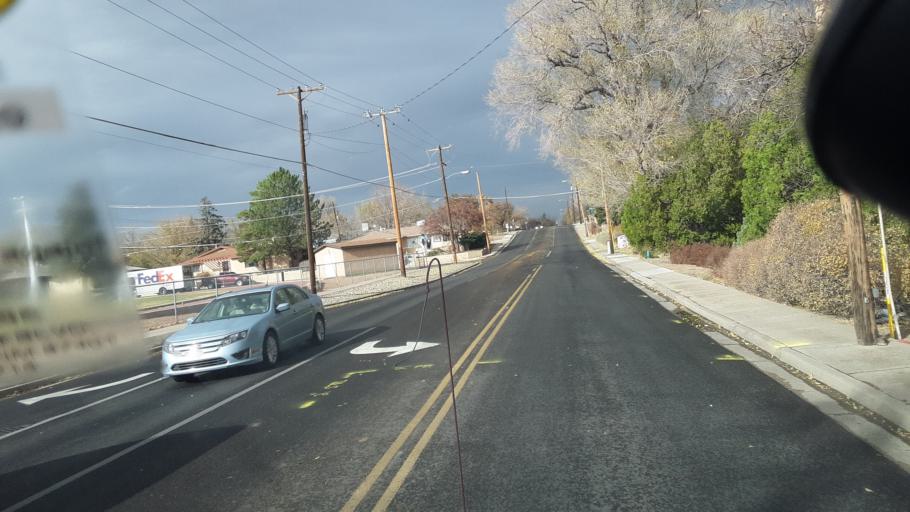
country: US
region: New Mexico
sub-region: San Juan County
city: Farmington
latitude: 36.7340
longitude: -108.1979
